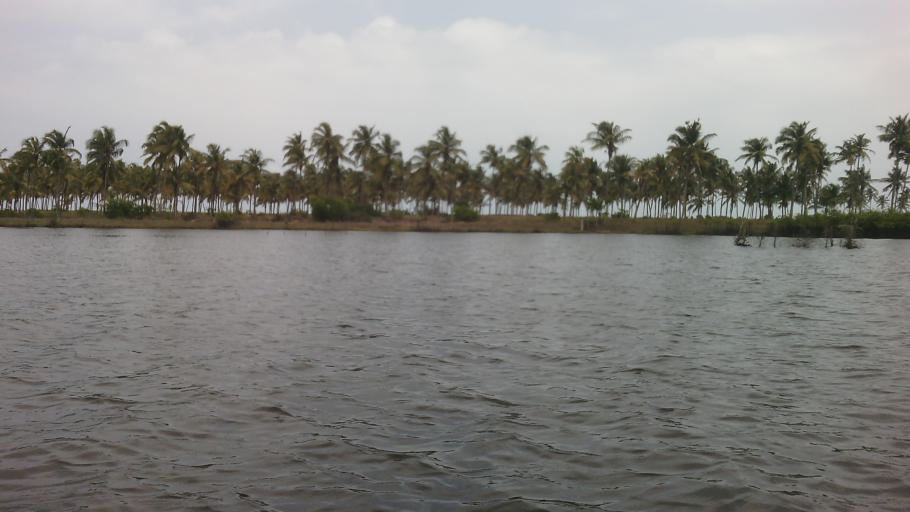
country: BJ
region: Atlantique
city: Ouidah
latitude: 6.3079
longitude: 1.9876
